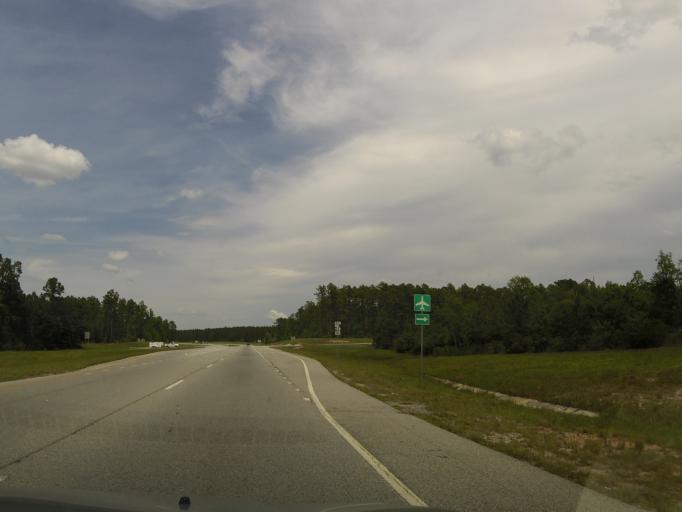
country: US
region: Georgia
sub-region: Emanuel County
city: Swainsboro
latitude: 32.6194
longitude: -82.3782
